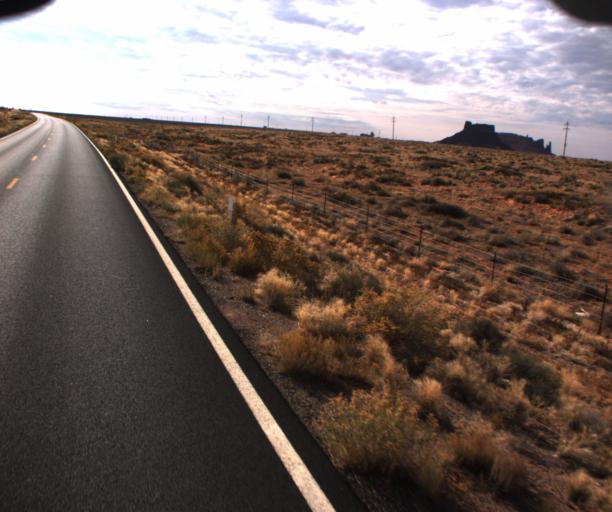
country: US
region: Arizona
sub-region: Apache County
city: Many Farms
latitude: 36.5642
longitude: -109.5427
